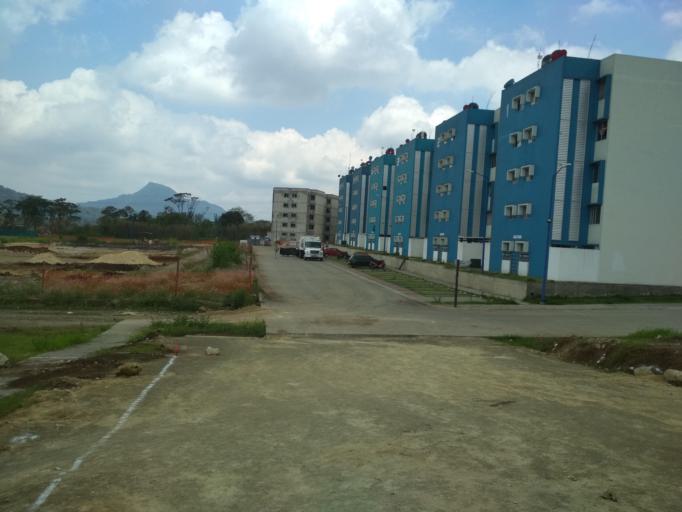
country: MX
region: Veracruz
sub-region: Ixtaczoquitlan
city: Buenavista
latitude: 18.8827
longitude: -97.0625
